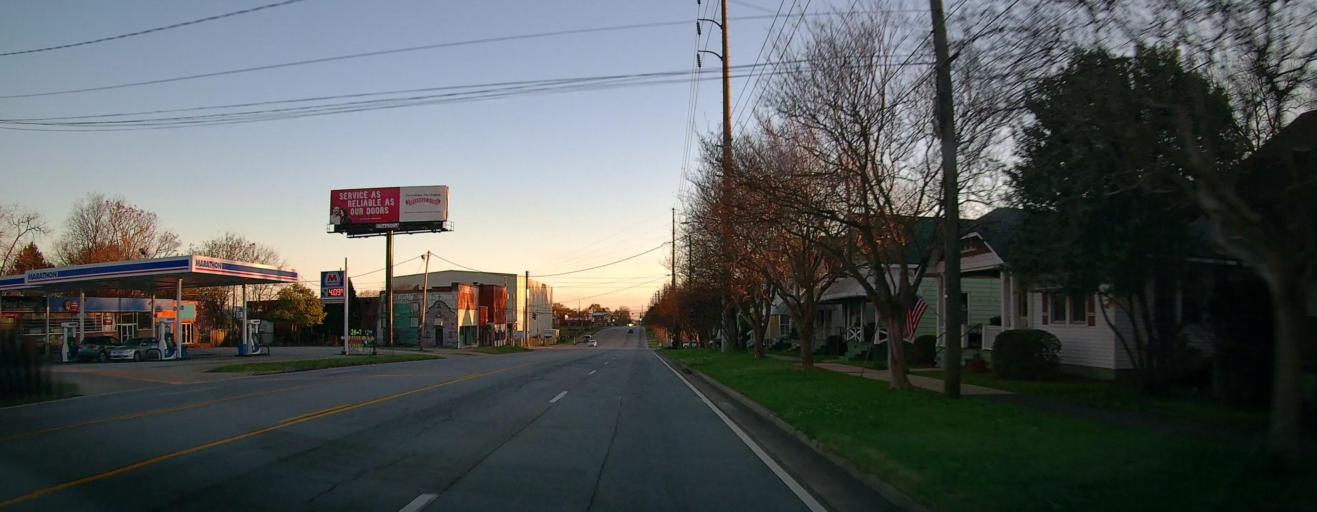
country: US
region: Alabama
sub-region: Russell County
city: Phenix City
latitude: 32.4977
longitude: -84.9902
